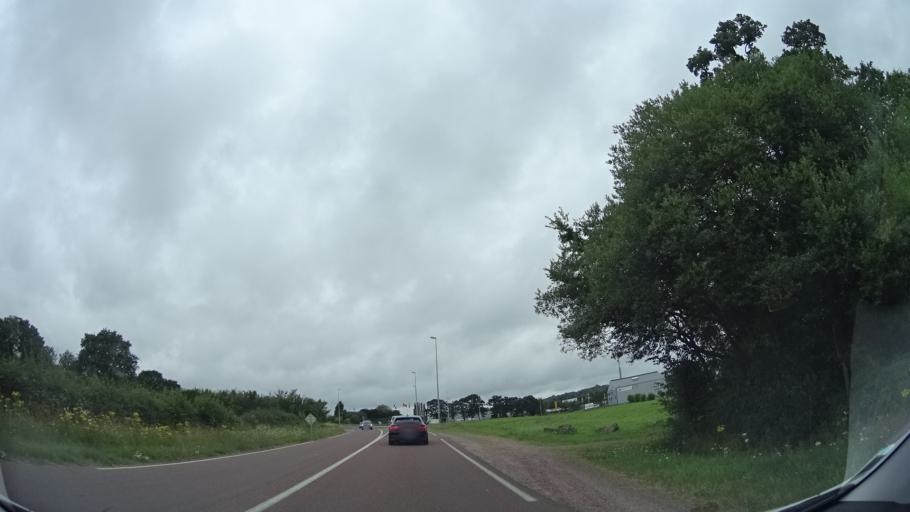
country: FR
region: Lower Normandy
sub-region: Departement de la Manche
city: La Haye-du-Puits
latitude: 49.2771
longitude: -1.5406
